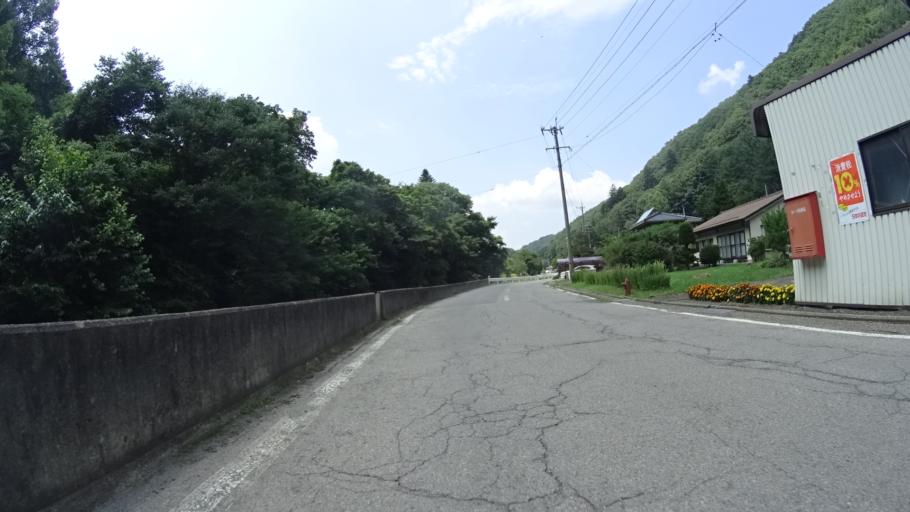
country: JP
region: Nagano
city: Saku
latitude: 36.1282
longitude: 138.5811
